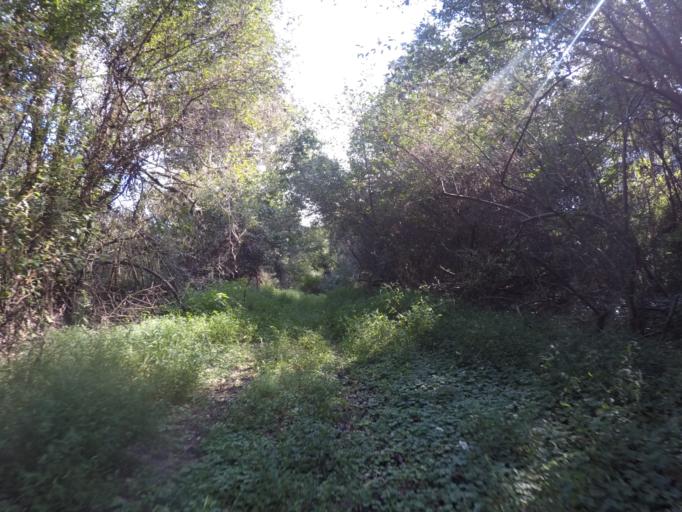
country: US
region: West Virginia
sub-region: Cabell County
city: Barboursville
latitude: 38.3660
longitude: -82.2707
